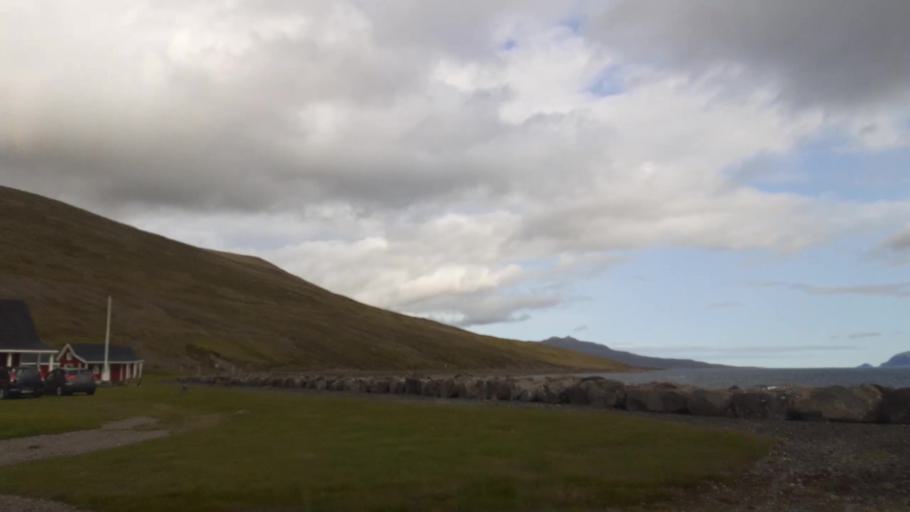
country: IS
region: East
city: Eskifjoerdur
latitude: 65.0596
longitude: -13.9938
